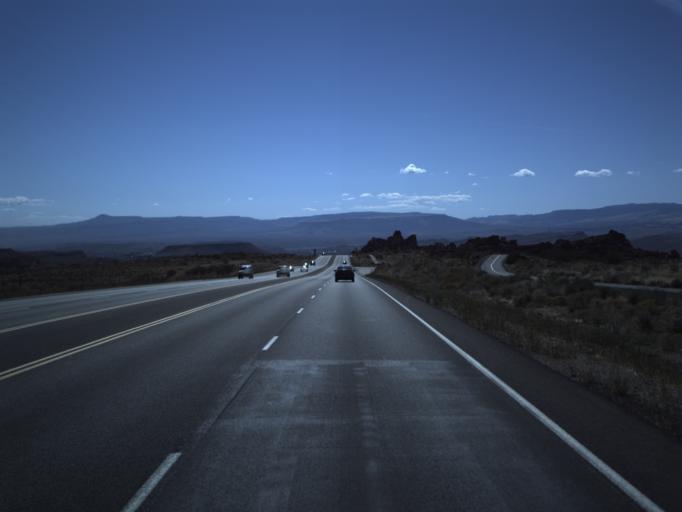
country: US
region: Utah
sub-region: Washington County
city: Santa Clara
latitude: 37.1798
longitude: -113.6191
